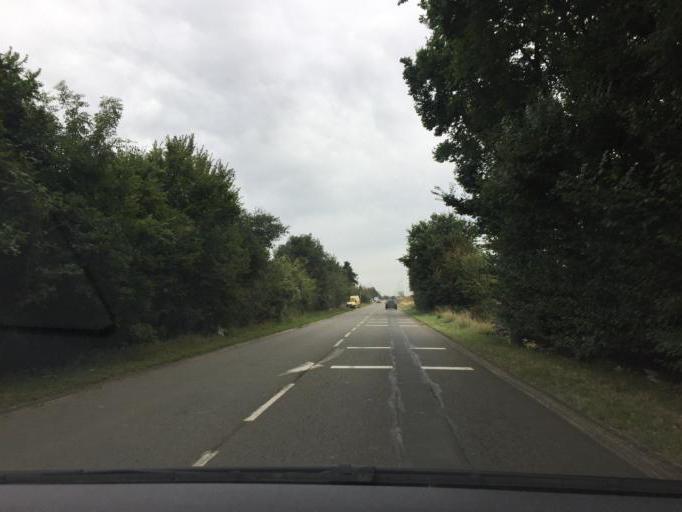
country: FR
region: Ile-de-France
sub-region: Departement des Yvelines
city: Les Loges-en-Josas
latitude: 48.7568
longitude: 2.1218
